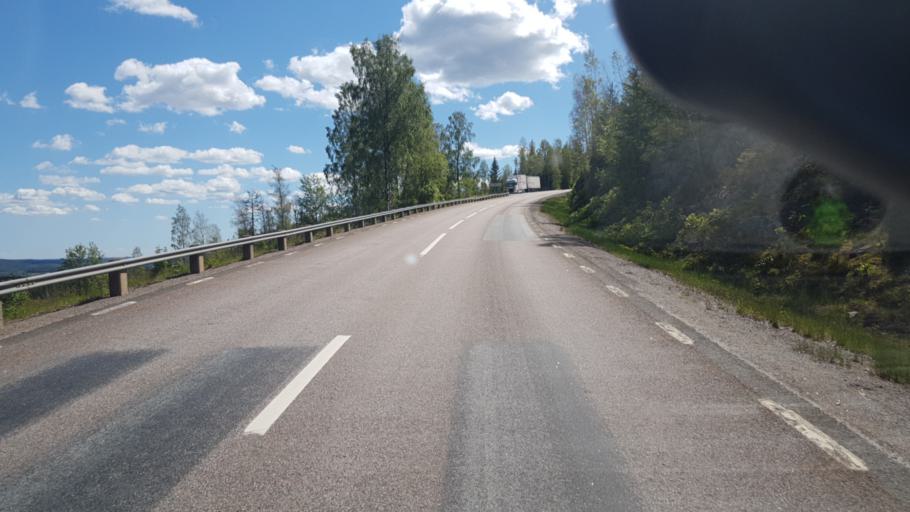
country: SE
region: Vaermland
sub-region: Sunne Kommun
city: Sunne
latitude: 59.7022
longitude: 13.1061
